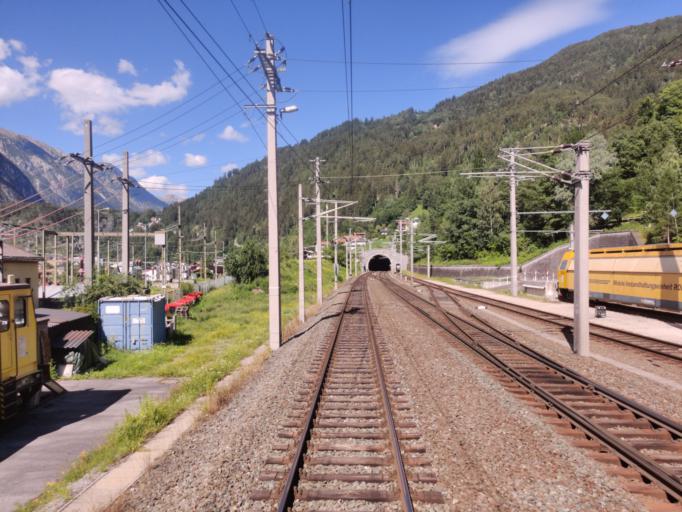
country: AT
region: Tyrol
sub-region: Politischer Bezirk Landeck
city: Zams
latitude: 47.1515
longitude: 10.5858
